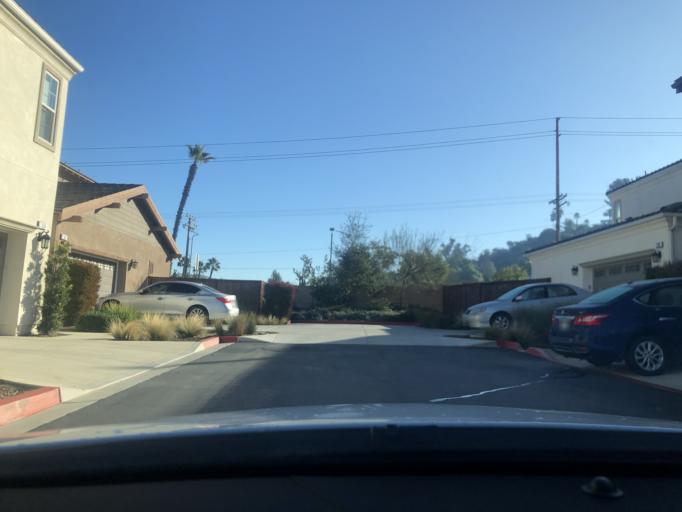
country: US
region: California
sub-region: San Diego County
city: Casa de Oro-Mount Helix
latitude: 32.7776
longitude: -116.9586
